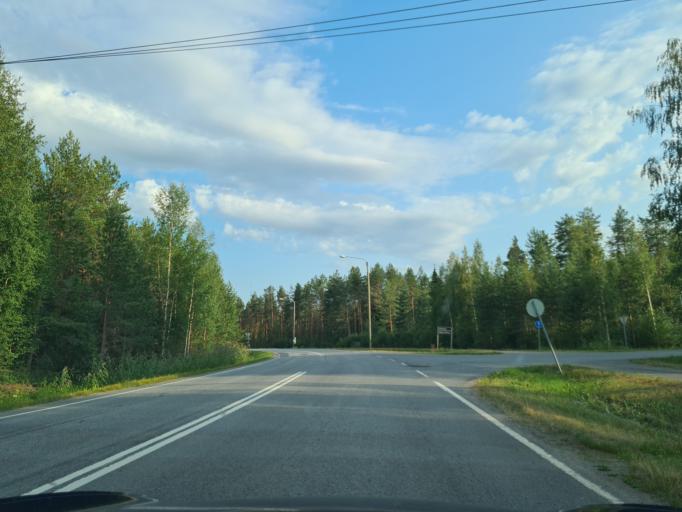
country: FI
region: Southern Ostrobothnia
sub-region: Seinaejoki
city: Lapua
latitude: 62.9860
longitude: 22.9393
